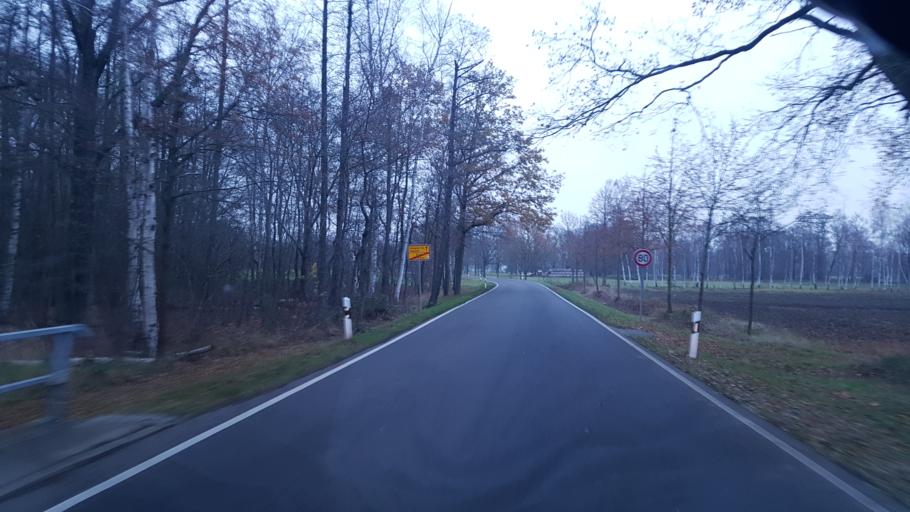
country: DE
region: Brandenburg
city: Burg
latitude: 51.8464
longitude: 14.1618
